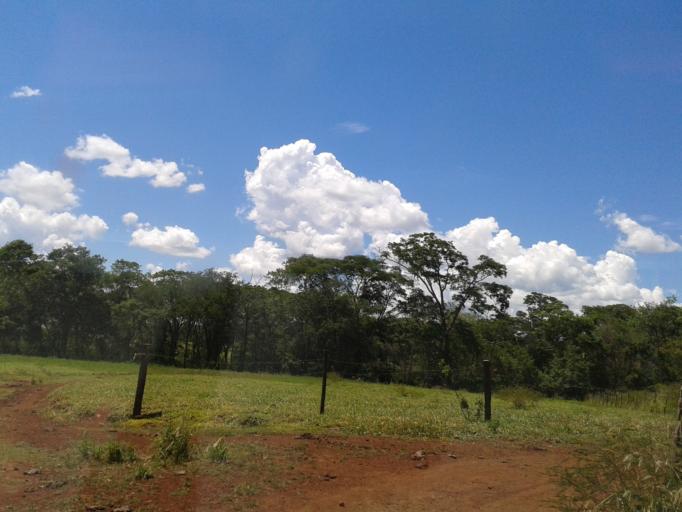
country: BR
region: Minas Gerais
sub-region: Centralina
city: Centralina
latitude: -18.6846
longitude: -49.1872
